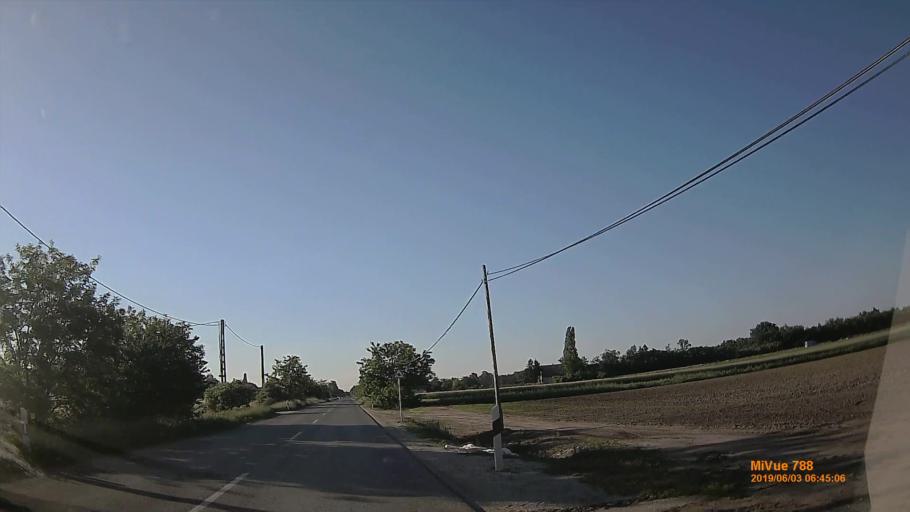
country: HU
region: Pest
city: Bugyi
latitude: 47.2404
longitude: 19.1328
